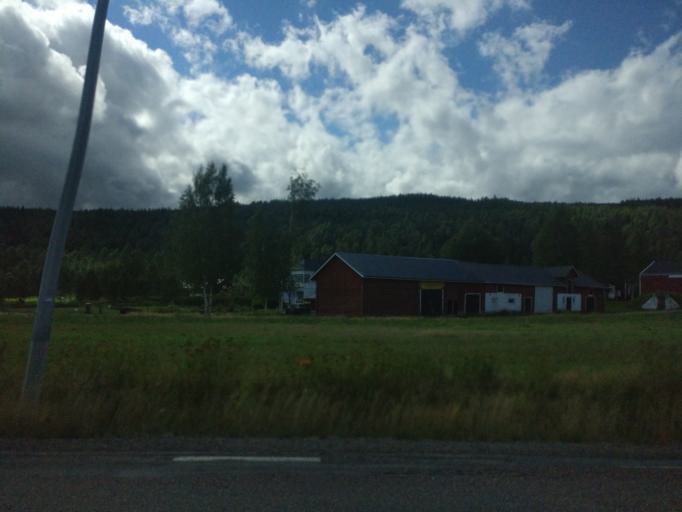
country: SE
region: Vaermland
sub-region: Hagfors Kommun
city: Ekshaerad
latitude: 60.2868
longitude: 13.3983
